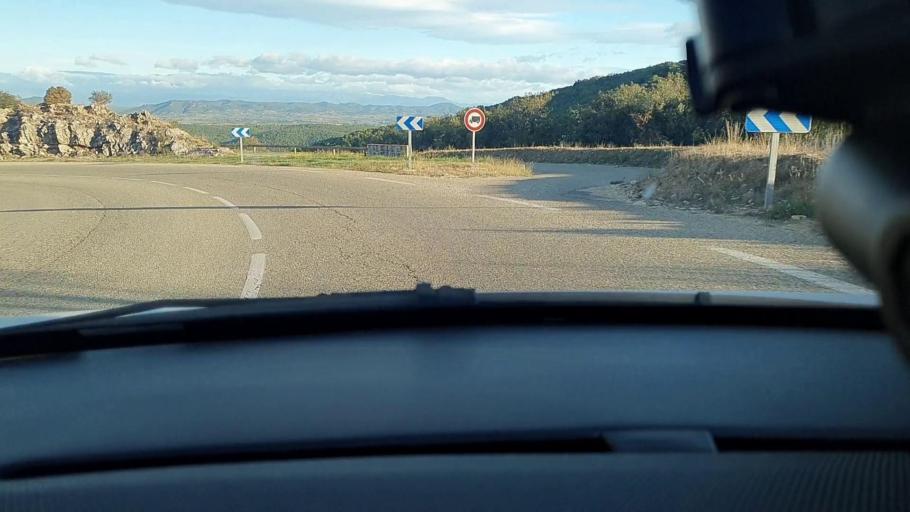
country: FR
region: Languedoc-Roussillon
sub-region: Departement du Gard
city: Barjac
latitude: 44.2292
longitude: 4.3184
